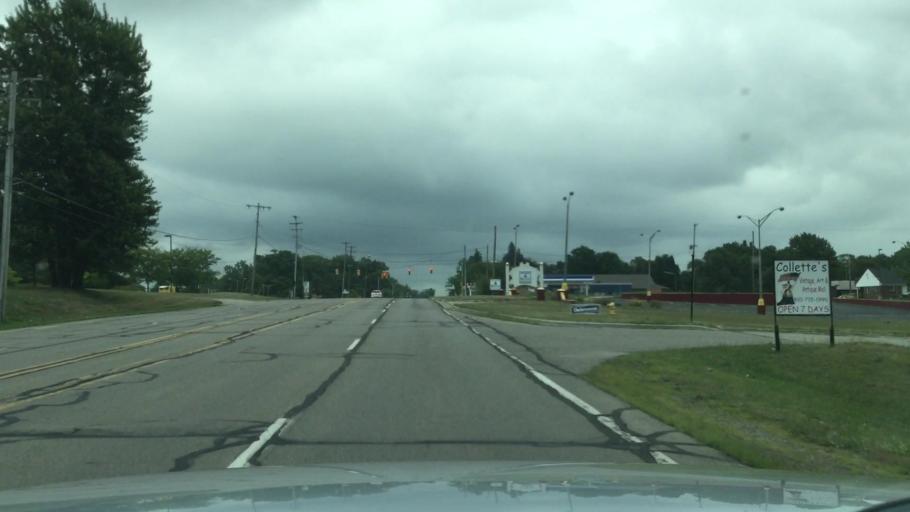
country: US
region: Michigan
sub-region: Genesee County
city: Burton
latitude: 43.0335
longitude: -83.5980
